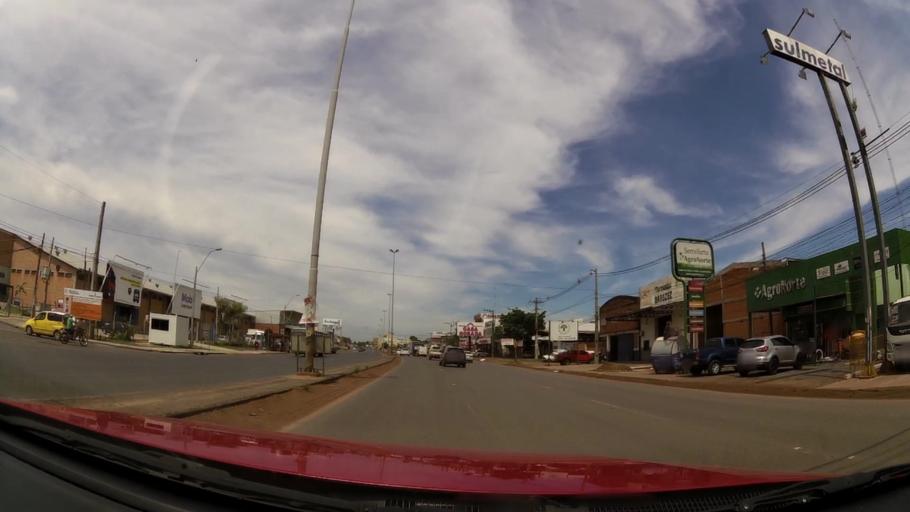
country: PY
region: Central
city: Colonia Mariano Roque Alonso
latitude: -25.2062
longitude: -57.5266
